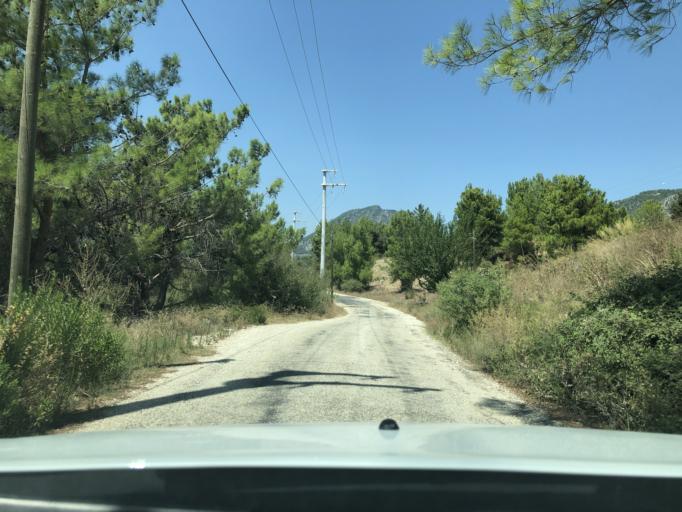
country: TR
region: Antalya
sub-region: Manavgat
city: Manavgat
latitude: 36.8725
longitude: 31.5514
